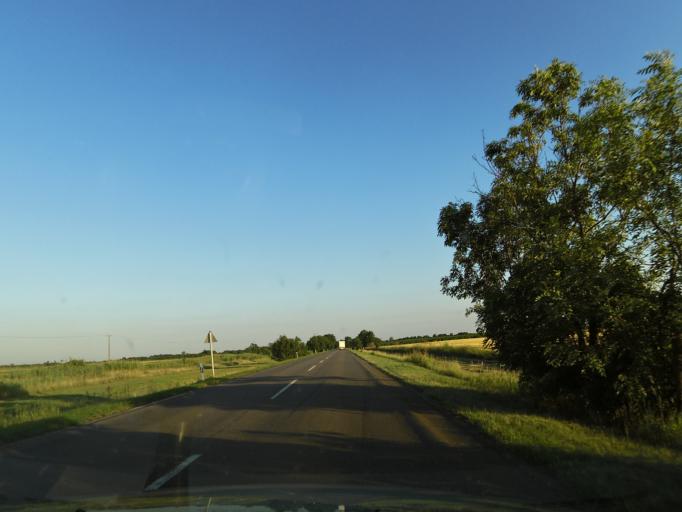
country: HU
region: Csongrad
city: Hodmezovasarhely
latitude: 46.5133
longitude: 20.3125
